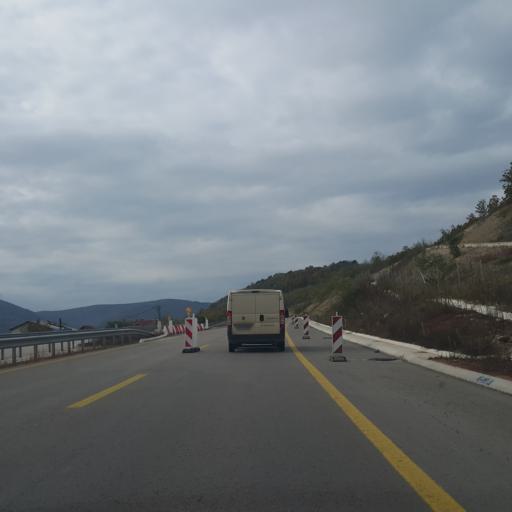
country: RS
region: Central Serbia
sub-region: Pirotski Okrug
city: Bela Palanka
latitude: 43.2354
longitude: 22.3081
